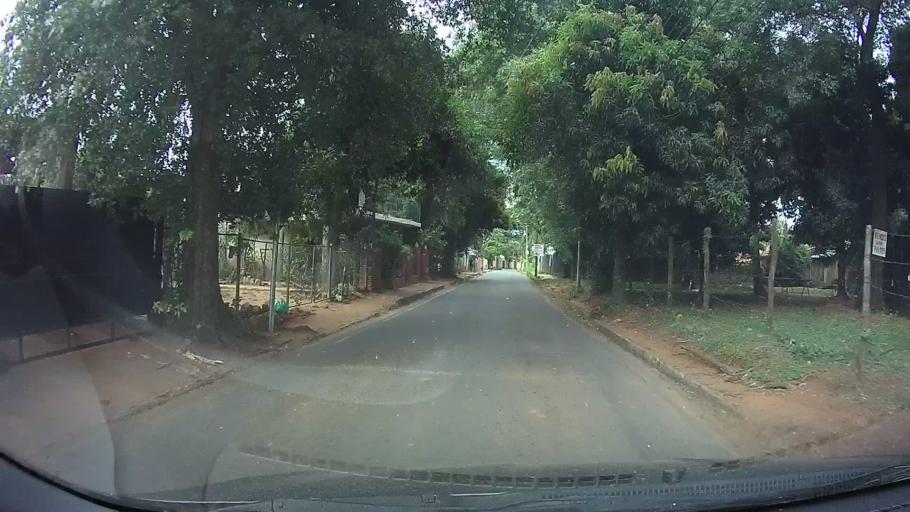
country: PY
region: Central
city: Fernando de la Mora
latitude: -25.3016
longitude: -57.5205
